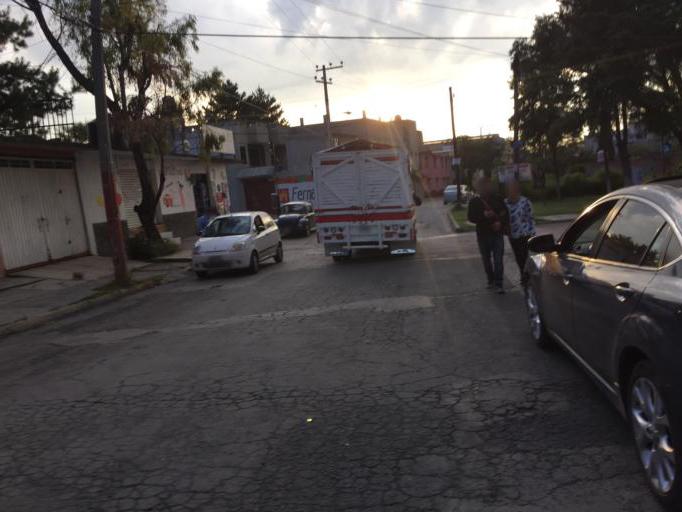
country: MX
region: Mexico
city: Cuautitlan Izcalli
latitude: 19.6661
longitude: -99.2178
